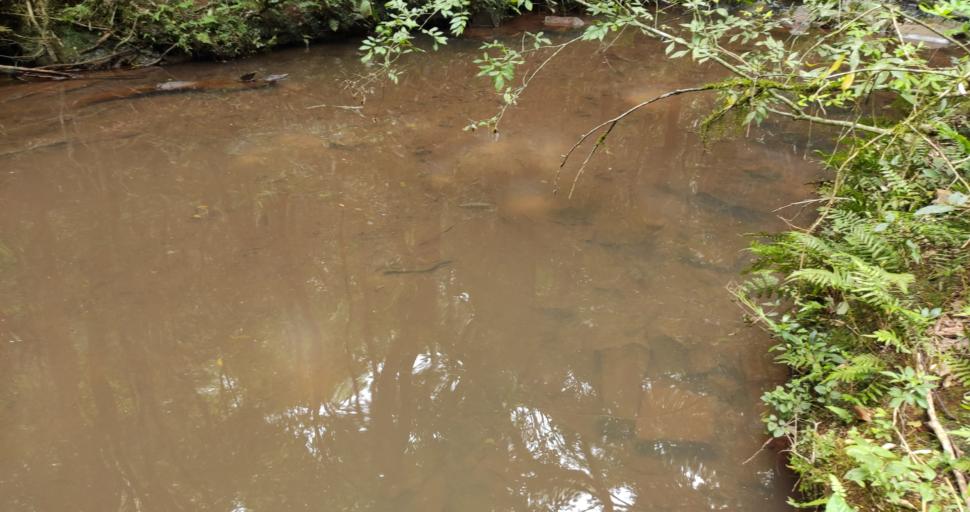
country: AR
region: Misiones
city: El Soberbio
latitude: -27.2743
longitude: -54.2203
